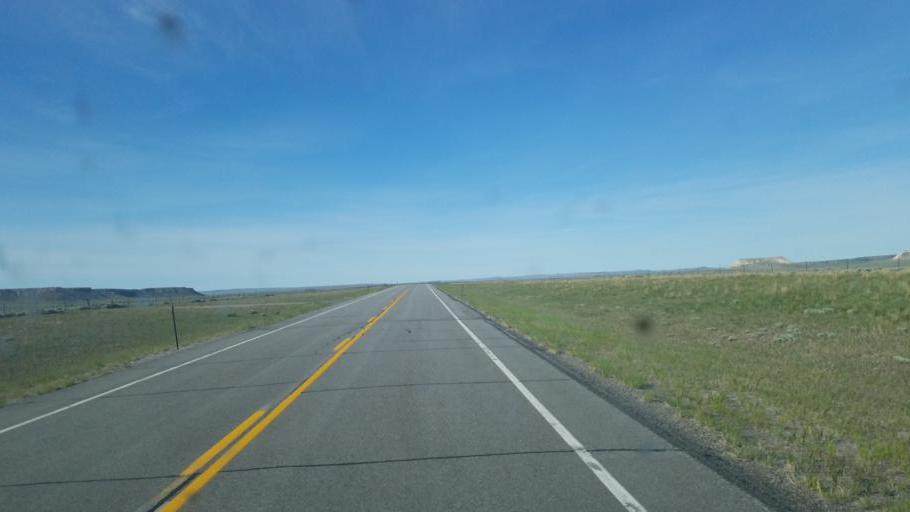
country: US
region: Wyoming
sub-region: Fremont County
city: Riverton
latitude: 42.6648
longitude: -108.1836
